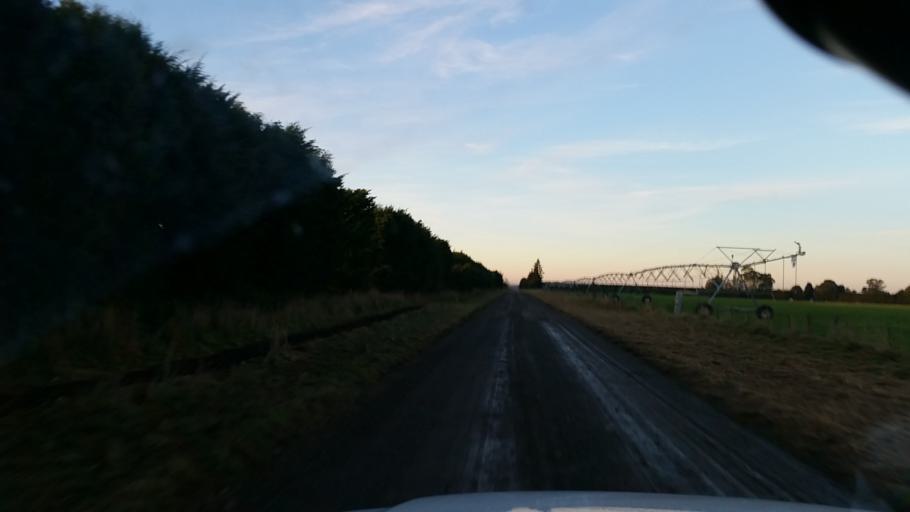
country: NZ
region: Canterbury
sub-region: Ashburton District
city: Methven
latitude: -43.7900
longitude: 171.5235
